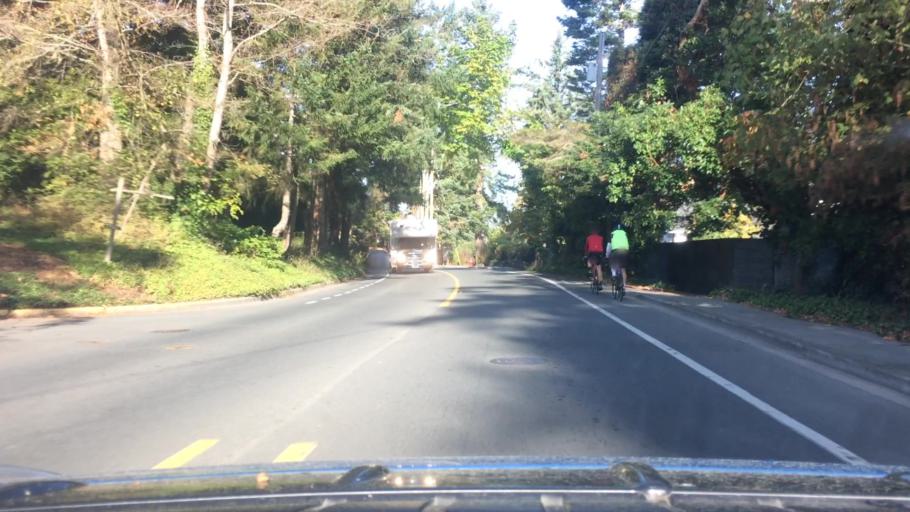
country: CA
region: British Columbia
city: Oak Bay
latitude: 48.5030
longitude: -123.3450
